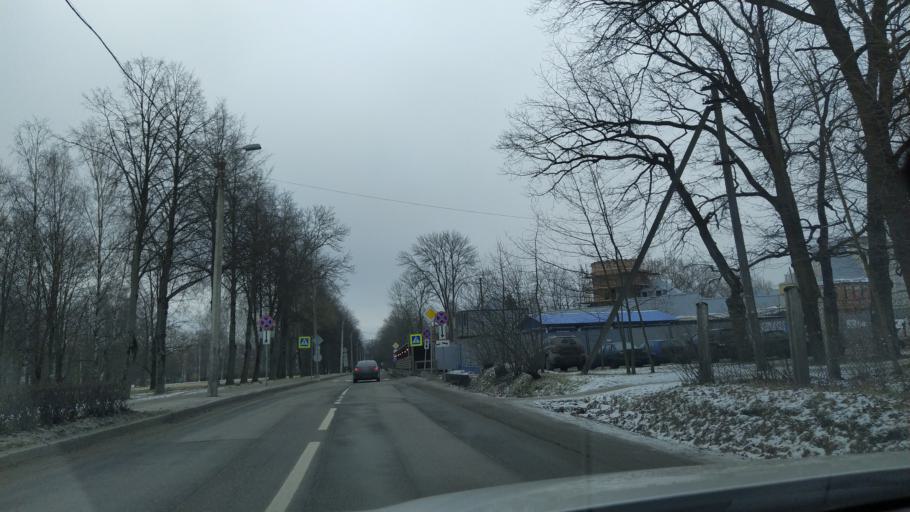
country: RU
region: St.-Petersburg
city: Pushkin
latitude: 59.7267
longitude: 30.3933
